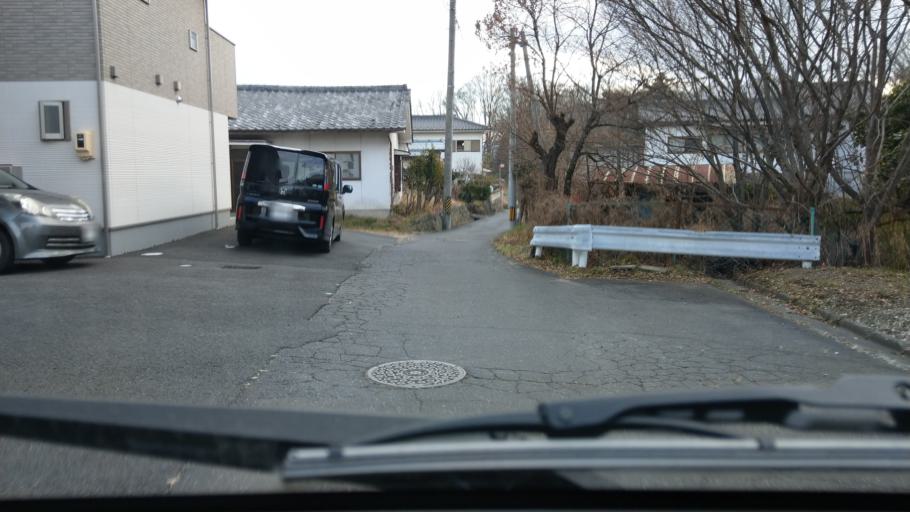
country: JP
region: Nagano
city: Komoro
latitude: 36.3239
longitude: 138.4223
